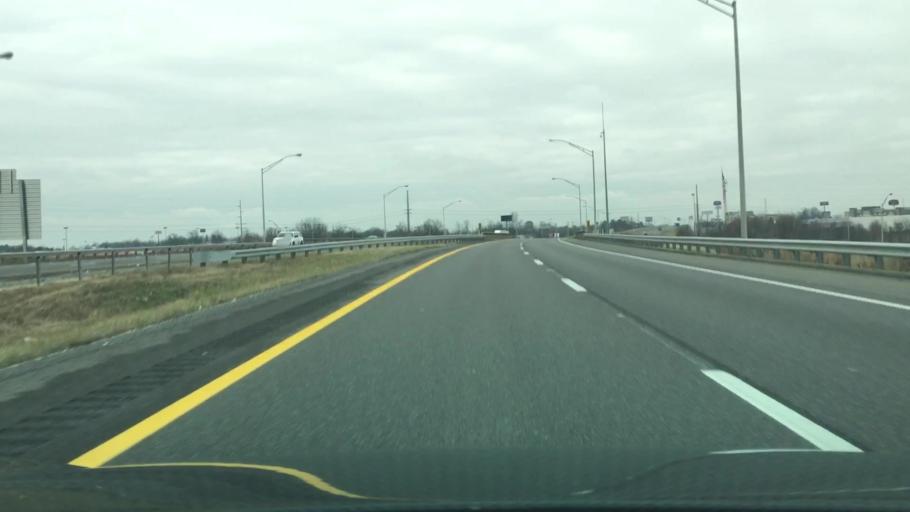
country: US
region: Kentucky
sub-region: McCracken County
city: Hendron
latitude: 37.0749
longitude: -88.6808
